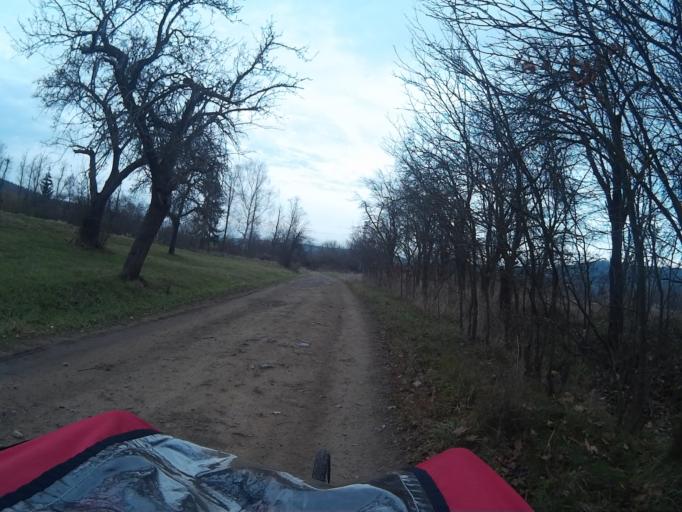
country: CZ
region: Plzensky
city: St'ahlavy
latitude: 49.6768
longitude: 13.4930
